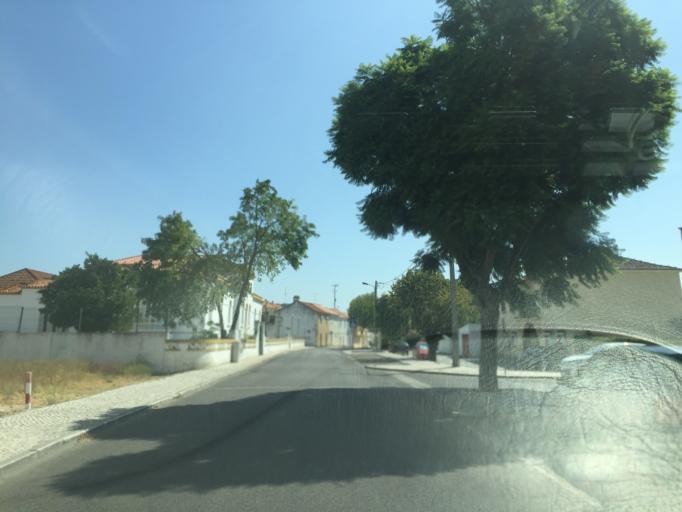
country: PT
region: Santarem
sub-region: Chamusca
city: Vila Nova da Barquinha
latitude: 39.4617
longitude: -8.4411
